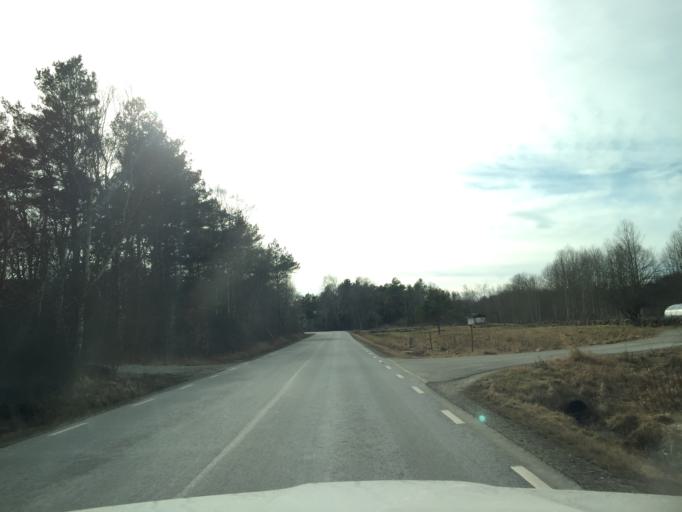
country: SE
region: Vaestra Goetaland
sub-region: Tjorns Kommun
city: Skaerhamn
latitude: 58.0299
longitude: 11.5417
